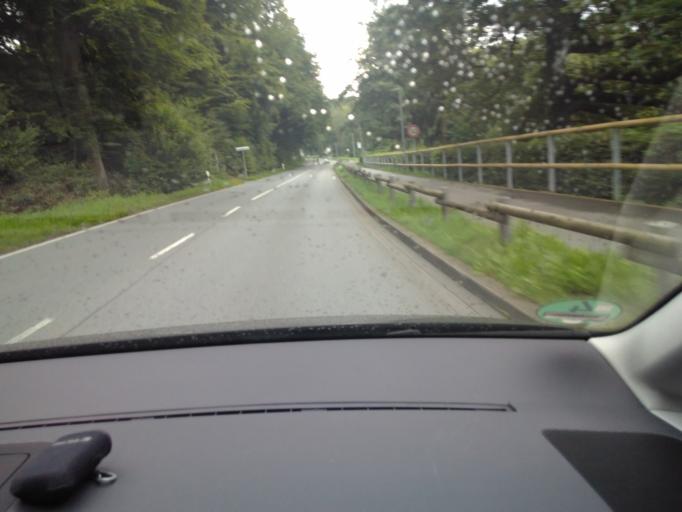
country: DE
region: North Rhine-Westphalia
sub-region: Regierungsbezirk Detmold
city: Bielefeld
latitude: 52.0227
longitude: 8.5045
